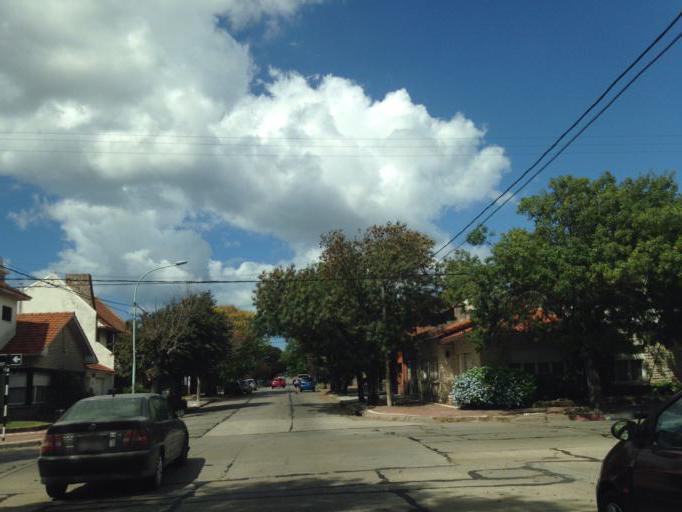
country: AR
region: Buenos Aires
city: Mar del Plata
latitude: -38.0176
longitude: -57.5619
